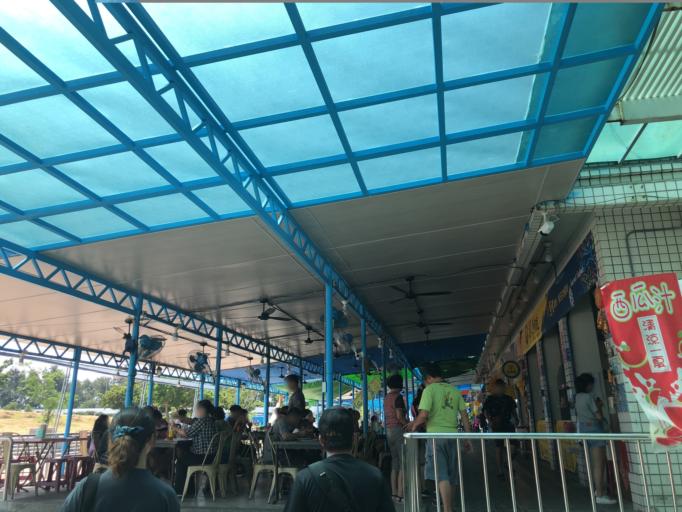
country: TW
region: Taiwan
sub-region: Chiayi
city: Taibao
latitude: 23.4513
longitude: 120.1354
